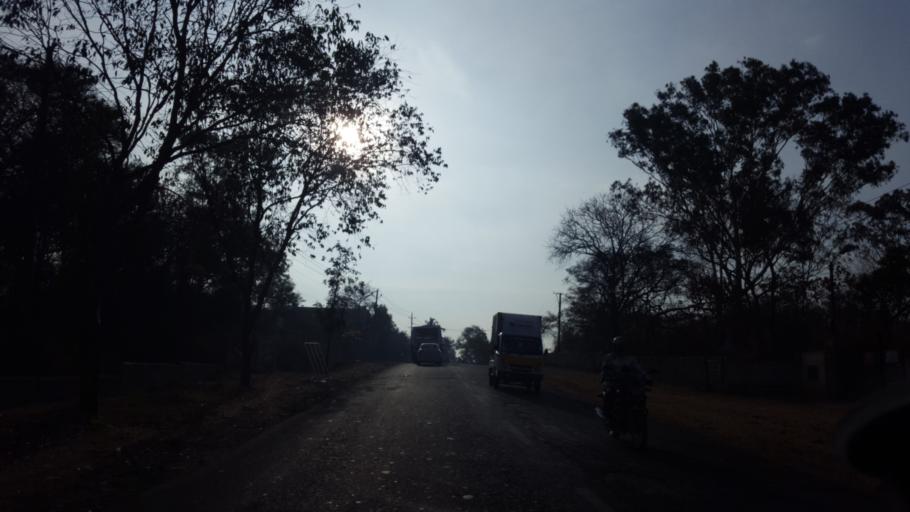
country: IN
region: Karnataka
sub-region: Bangalore Urban
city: Bangalore
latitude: 12.9059
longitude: 77.5017
